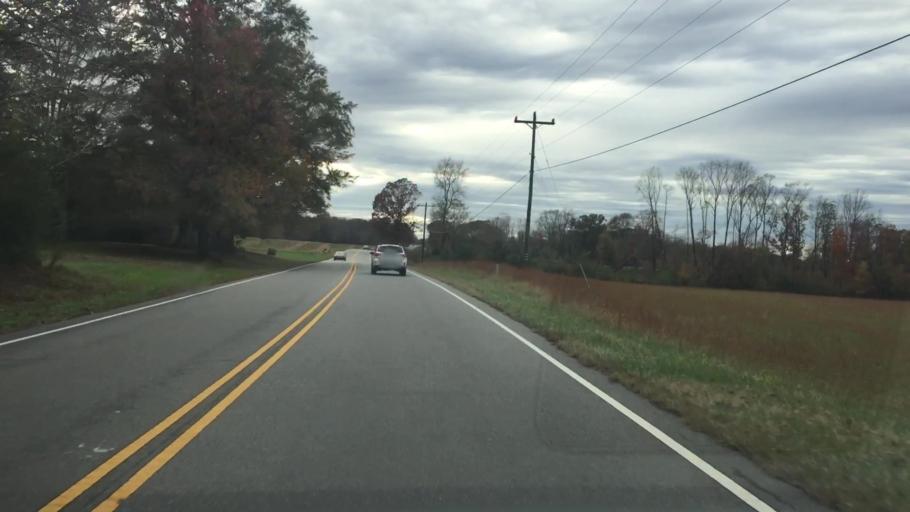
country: US
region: North Carolina
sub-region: Guilford County
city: Summerfield
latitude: 36.2772
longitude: -79.8117
